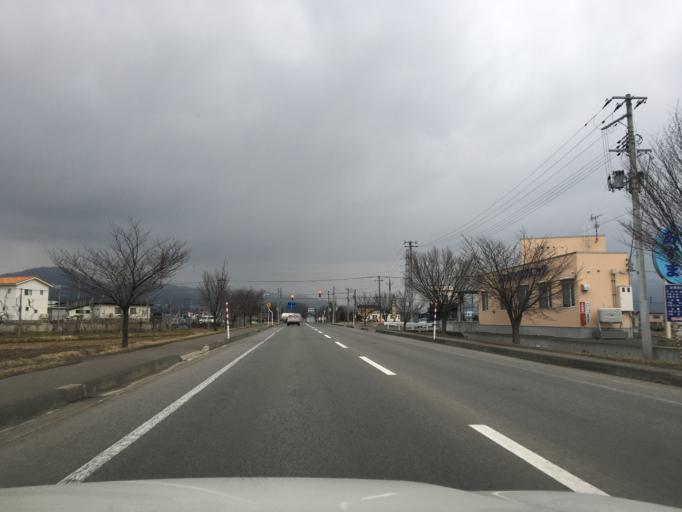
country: JP
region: Aomori
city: Kuroishi
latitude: 40.5766
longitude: 140.5684
